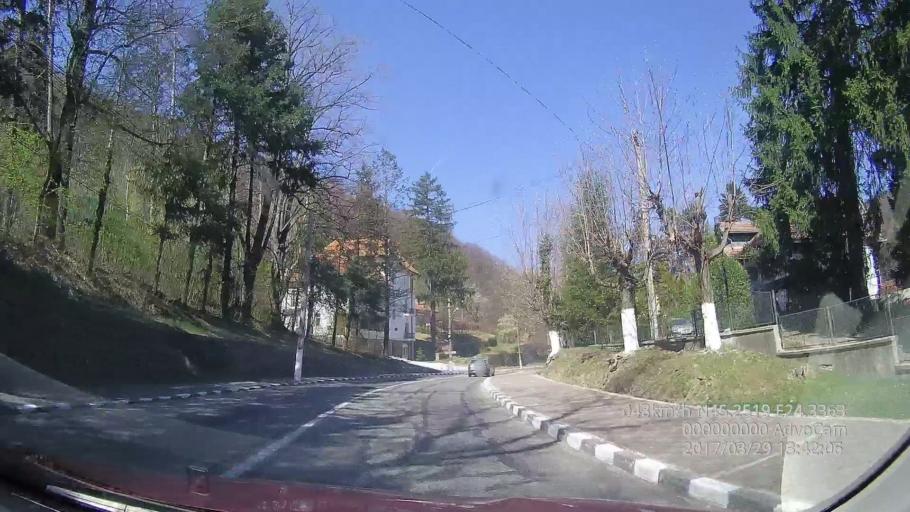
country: RO
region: Valcea
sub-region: Oras Calimanesti
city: Jiblea Veche
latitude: 45.2520
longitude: 24.3360
